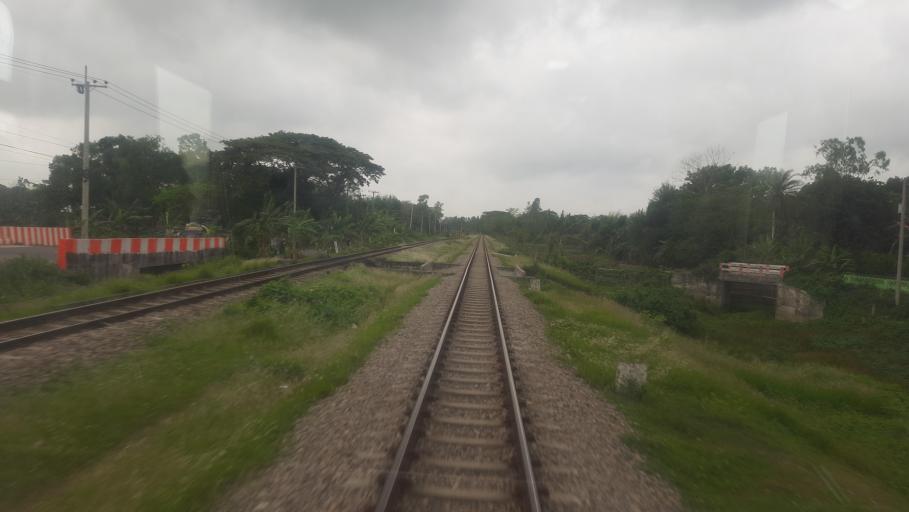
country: BD
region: Dhaka
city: Narsingdi
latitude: 23.9636
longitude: 90.8136
